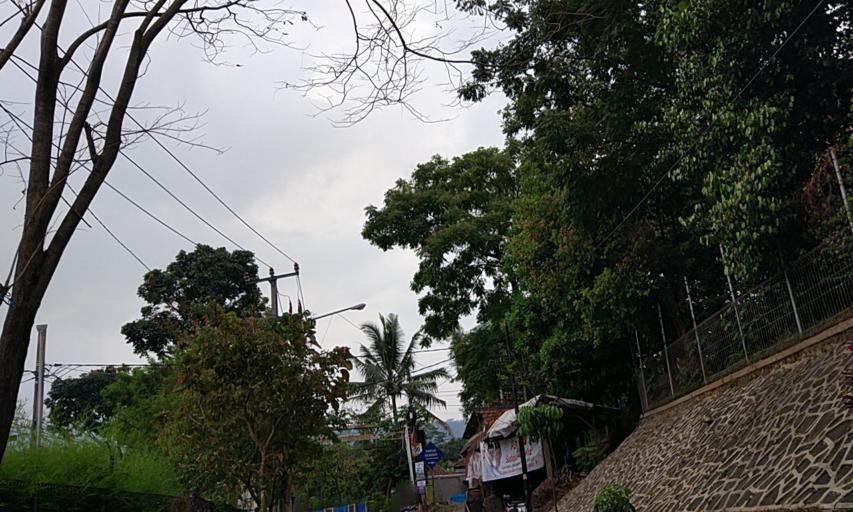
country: ID
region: West Java
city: Bandung
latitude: -6.8938
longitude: 107.6836
